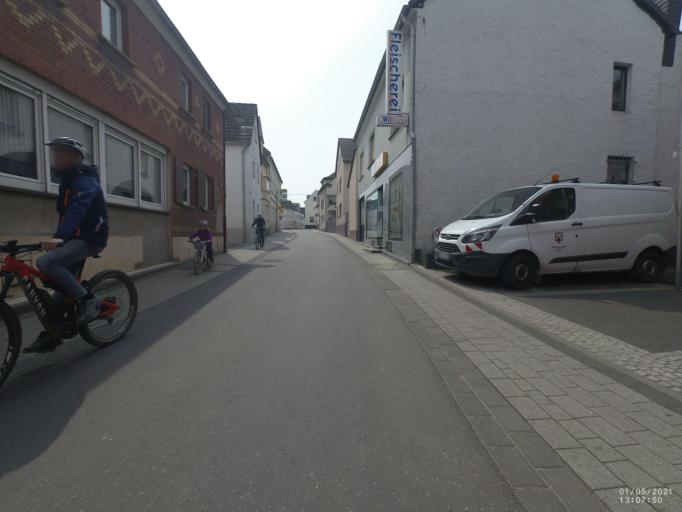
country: DE
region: Rheinland-Pfalz
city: Kettig
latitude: 50.3978
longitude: 7.4612
